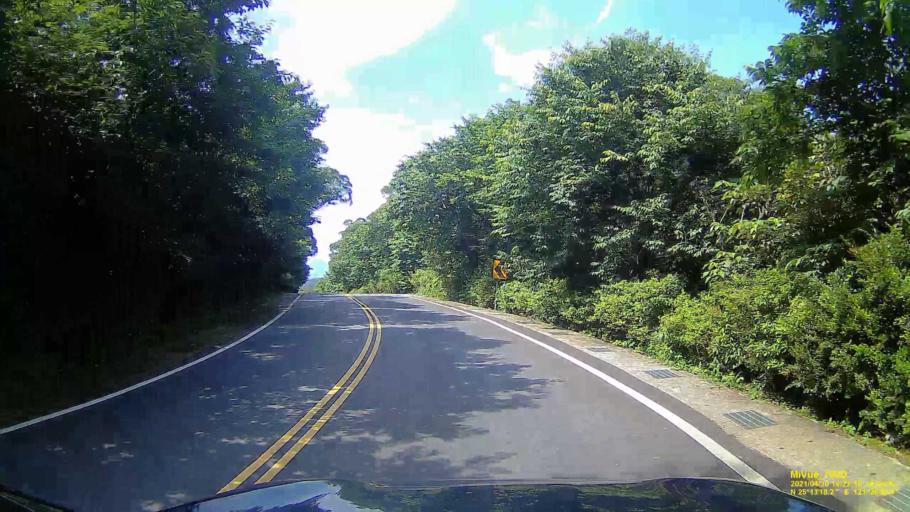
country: TW
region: Taipei
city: Taipei
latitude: 25.2221
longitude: 121.5142
